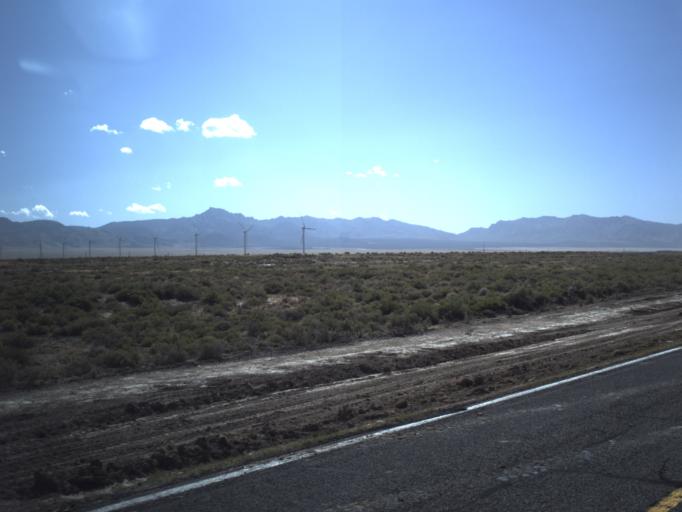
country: US
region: Utah
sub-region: Beaver County
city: Milford
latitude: 38.5238
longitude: -112.9912
